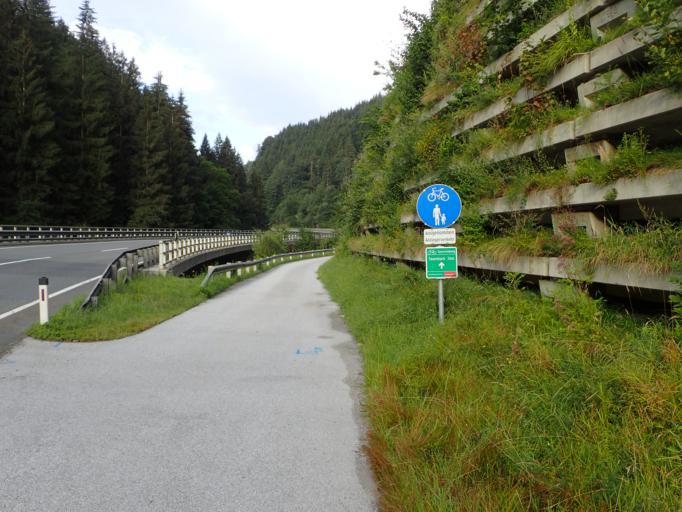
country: AT
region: Salzburg
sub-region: Politischer Bezirk Zell am See
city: Taxenbach
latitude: 47.3018
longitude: 12.9990
